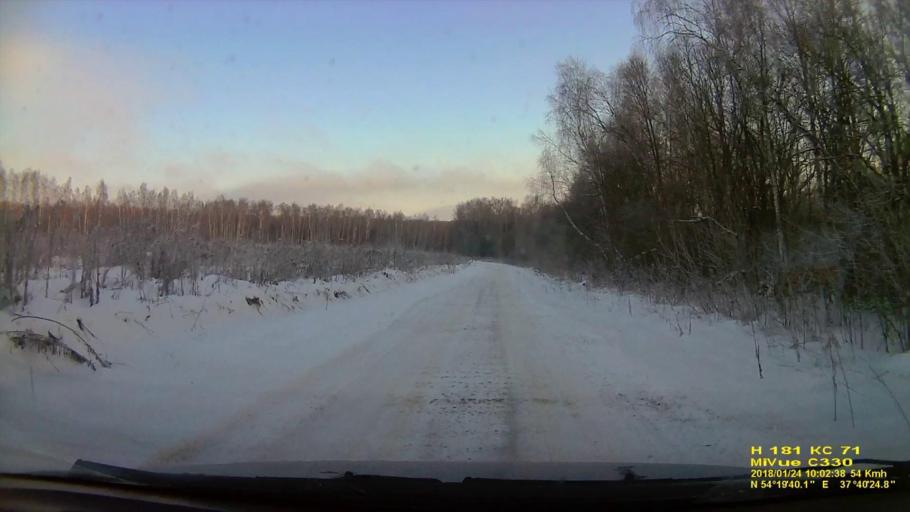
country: RU
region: Tula
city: Revyakino
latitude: 54.3279
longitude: 37.6737
